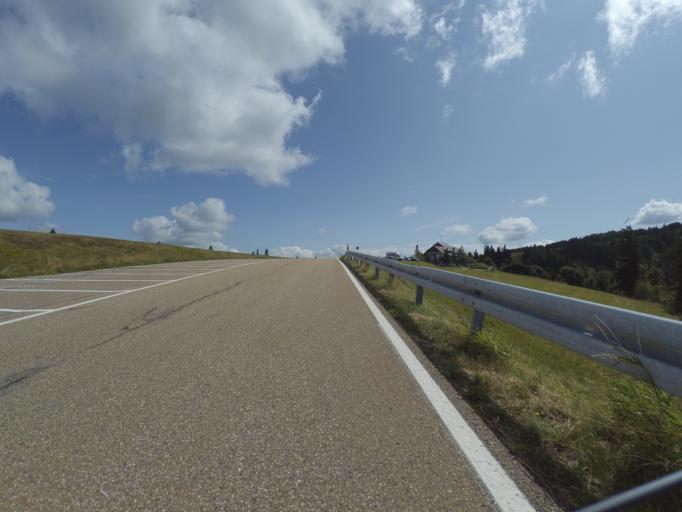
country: DE
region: Baden-Wuerttemberg
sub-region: Freiburg Region
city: Glottertal
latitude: 48.0666
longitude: 8.0155
